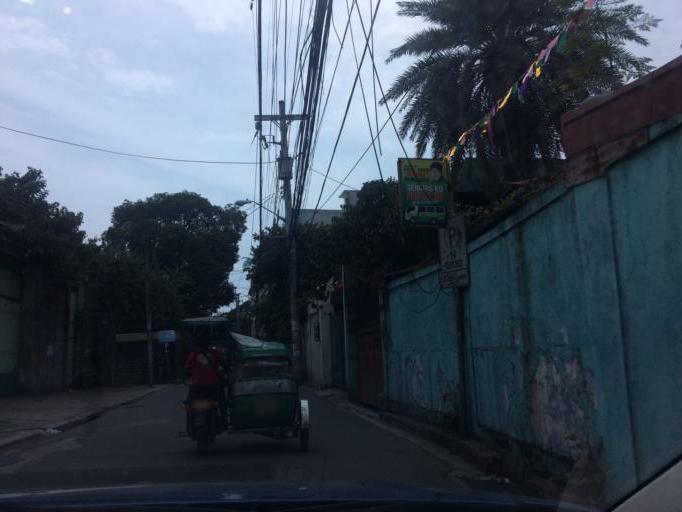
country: PH
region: Metro Manila
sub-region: Makati City
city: Makati City
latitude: 14.5432
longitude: 121.0045
